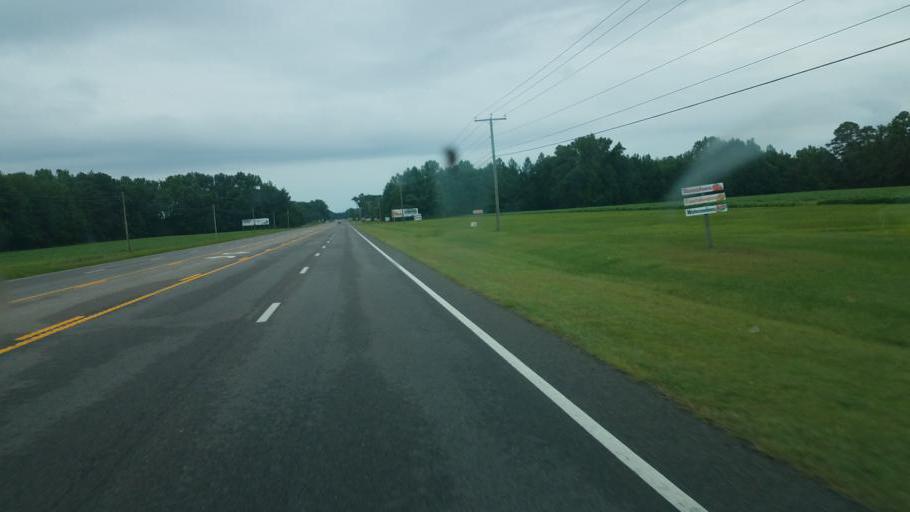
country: US
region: North Carolina
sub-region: Currituck County
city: Currituck
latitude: 36.2799
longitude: -75.9145
